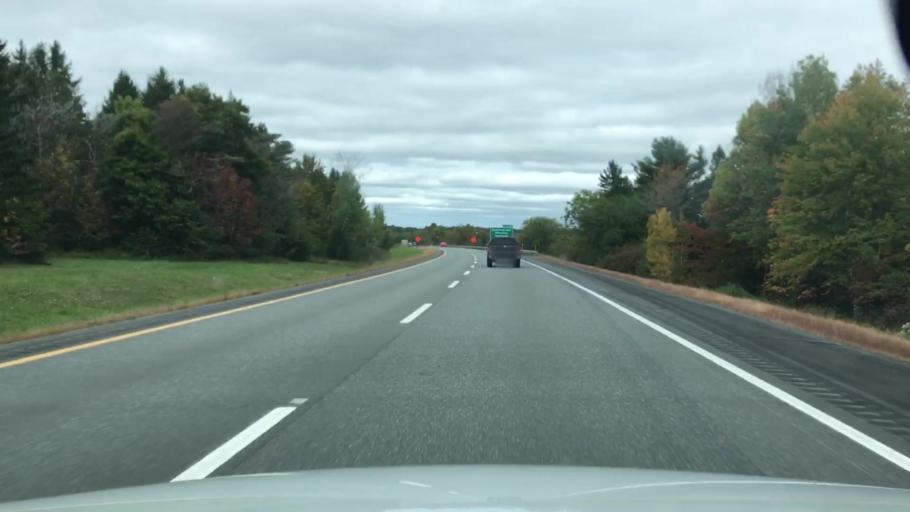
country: US
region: Maine
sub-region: Somerset County
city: Pittsfield
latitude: 44.7663
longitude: -69.4115
